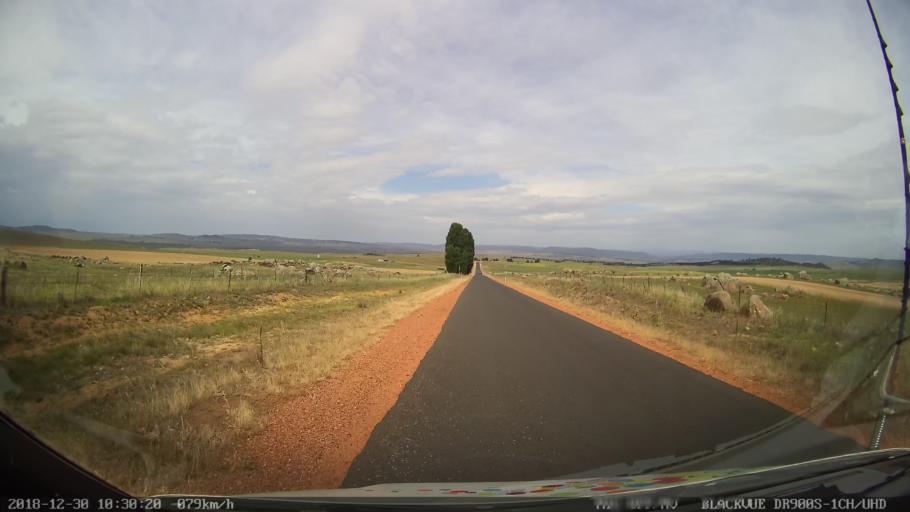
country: AU
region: New South Wales
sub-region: Snowy River
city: Berridale
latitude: -36.5035
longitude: 148.8967
